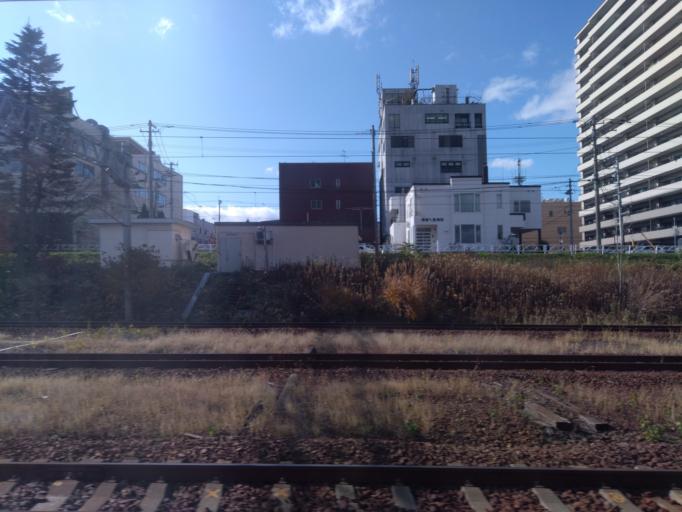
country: JP
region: Hokkaido
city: Kitahiroshima
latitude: 42.9801
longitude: 141.5632
